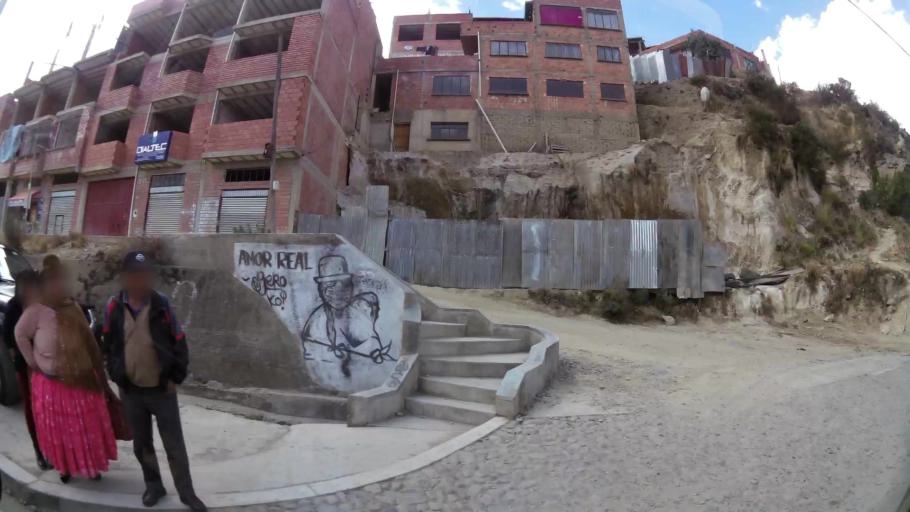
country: BO
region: La Paz
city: La Paz
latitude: -16.4692
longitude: -68.1212
